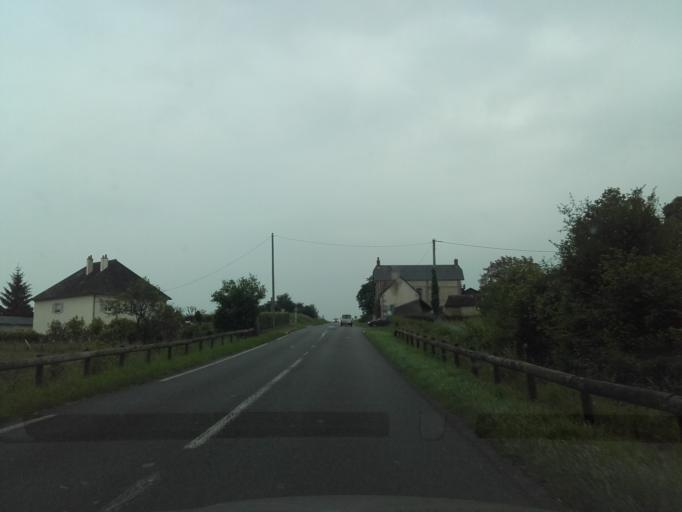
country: FR
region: Centre
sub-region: Departement d'Indre-et-Loire
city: Neuvy-le-Roi
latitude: 47.6551
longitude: 0.6491
